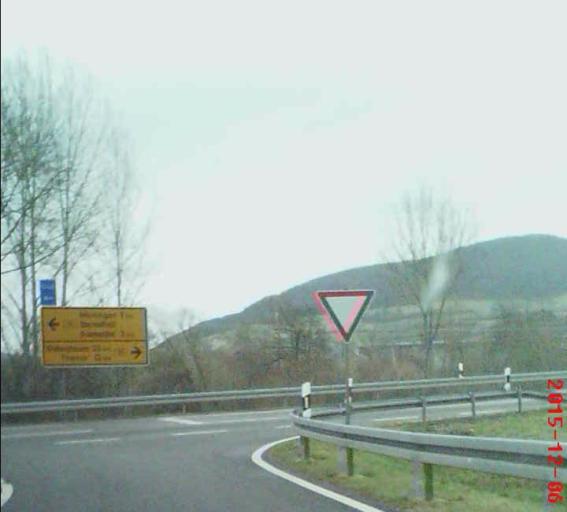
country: DE
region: Thuringia
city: Einhausen
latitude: 50.5230
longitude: 10.4683
